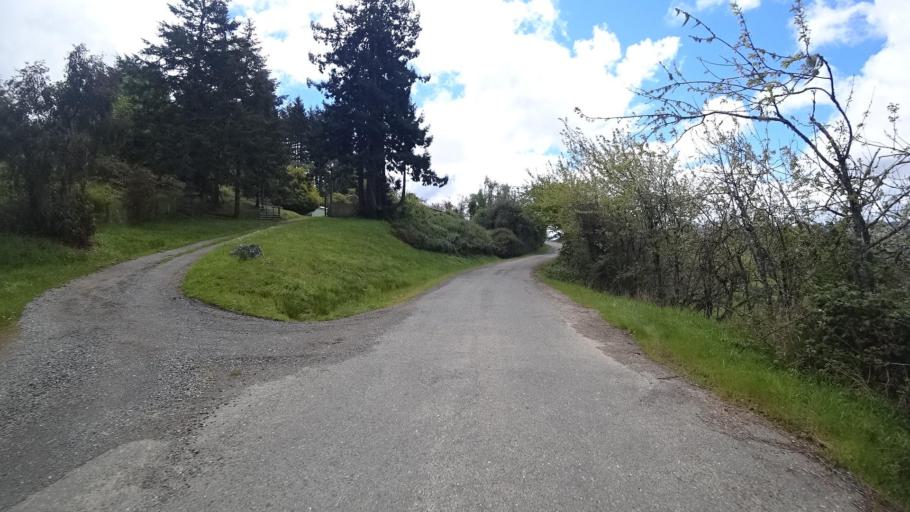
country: US
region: California
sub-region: Humboldt County
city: Blue Lake
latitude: 40.8556
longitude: -123.9242
